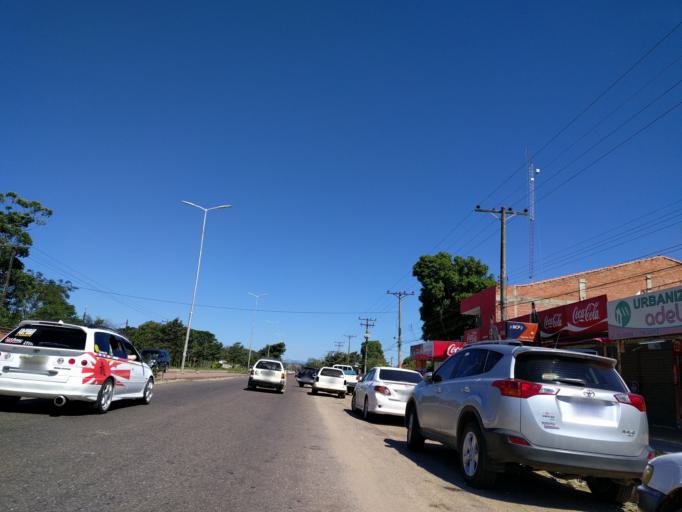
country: BO
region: Santa Cruz
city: Santa Cruz de la Sierra
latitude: -17.8632
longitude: -63.2665
